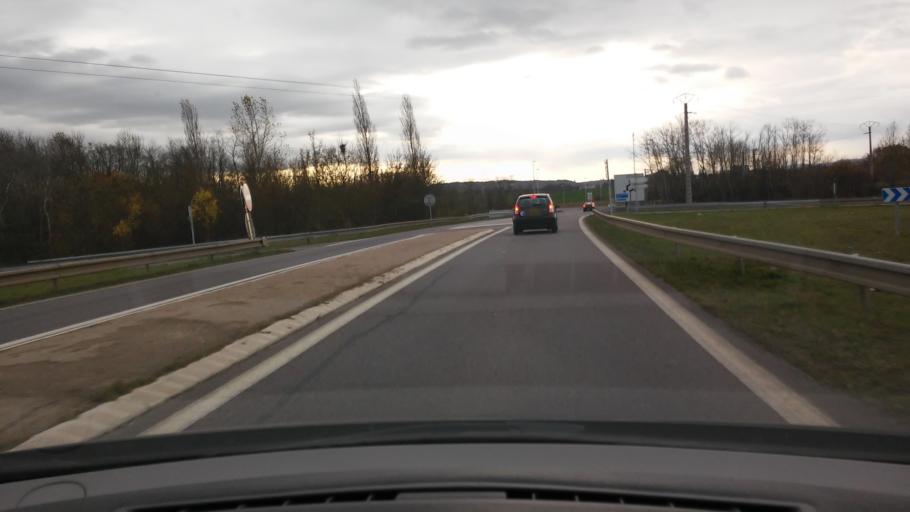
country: FR
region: Lorraine
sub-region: Departement de la Moselle
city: Argancy
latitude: 49.1988
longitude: 6.2088
